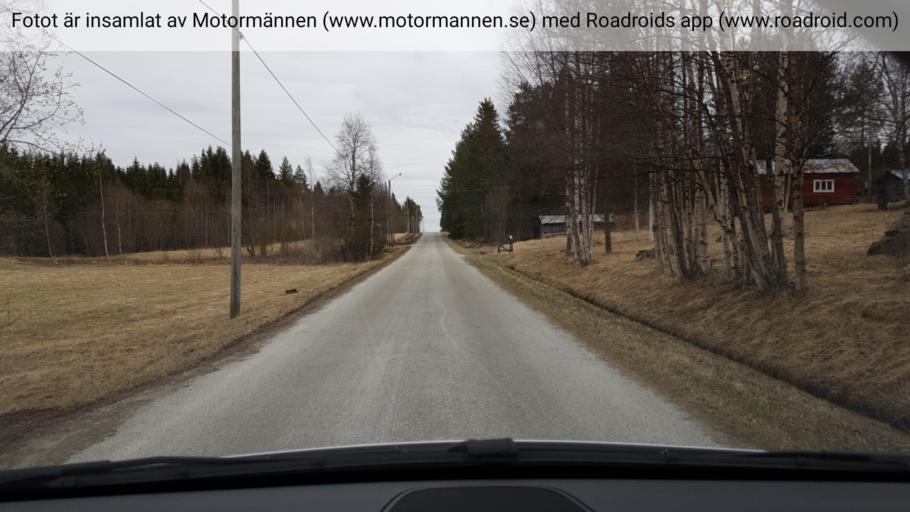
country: SE
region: Jaemtland
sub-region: Bergs Kommun
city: Hoverberg
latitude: 62.8426
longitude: 14.4361
